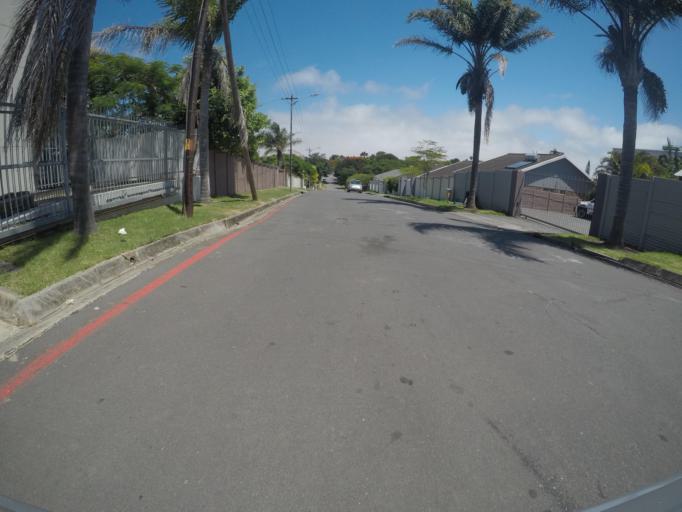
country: ZA
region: Eastern Cape
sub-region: Buffalo City Metropolitan Municipality
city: East London
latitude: -32.9849
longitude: 27.9075
